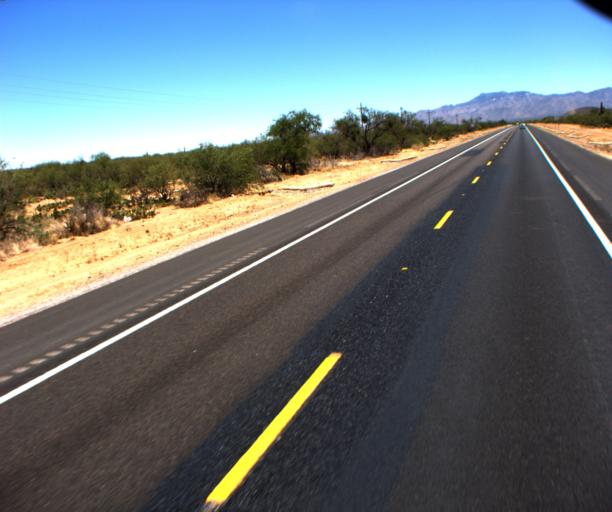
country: US
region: Arizona
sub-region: Pima County
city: Sells
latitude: 31.9185
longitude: -111.8376
